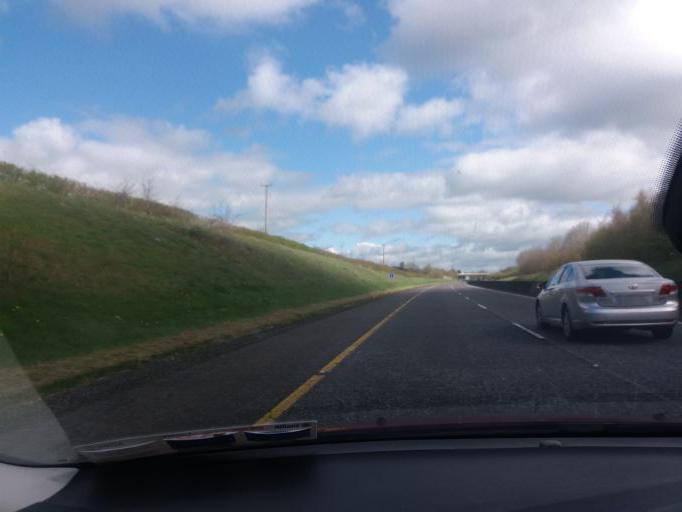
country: IE
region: Munster
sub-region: County Cork
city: Rathcormac
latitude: 52.0759
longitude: -8.3014
